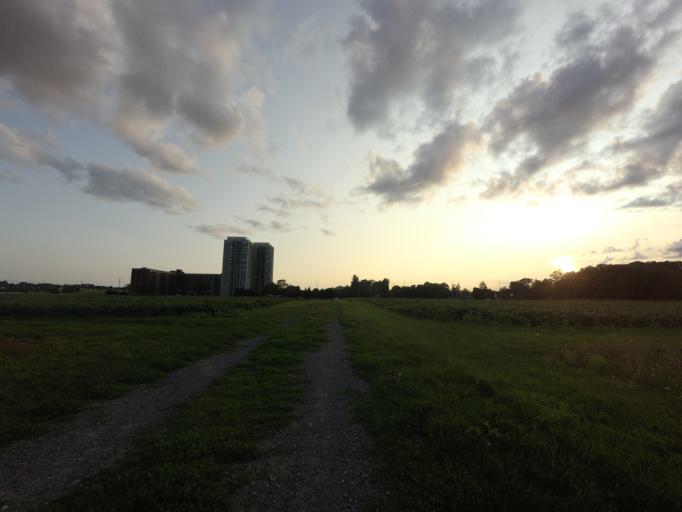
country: CA
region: Ontario
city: Ottawa
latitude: 45.3799
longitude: -75.7180
